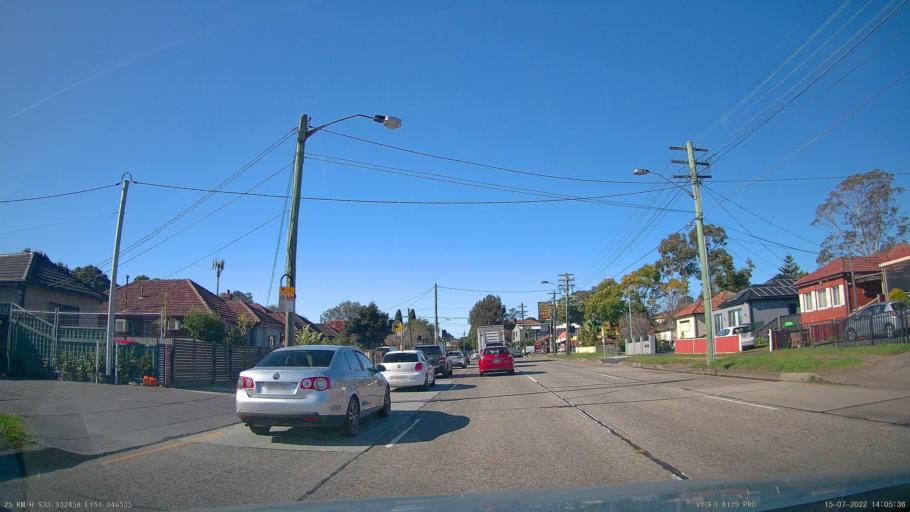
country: AU
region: New South Wales
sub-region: Bankstown
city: Bankstown
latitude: -33.9325
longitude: 151.0486
